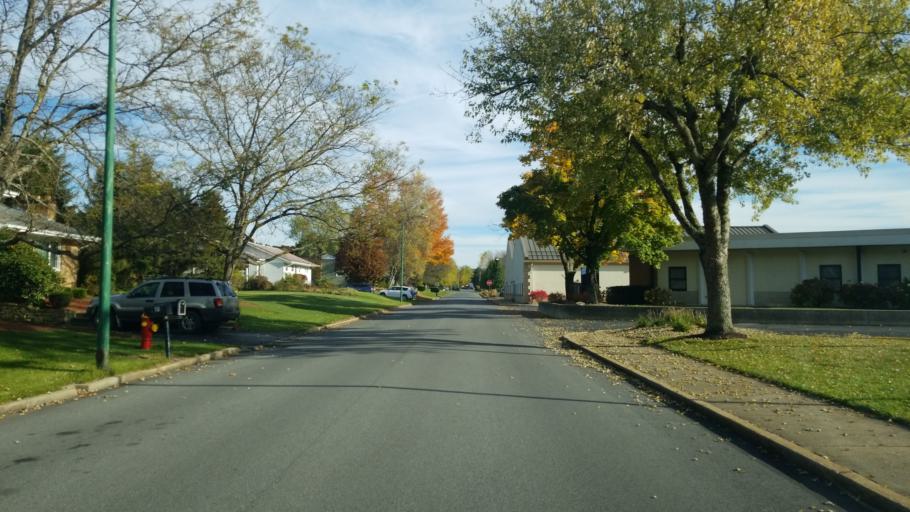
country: US
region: Pennsylvania
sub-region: Jefferson County
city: Brockway
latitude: 41.2513
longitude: -78.7903
